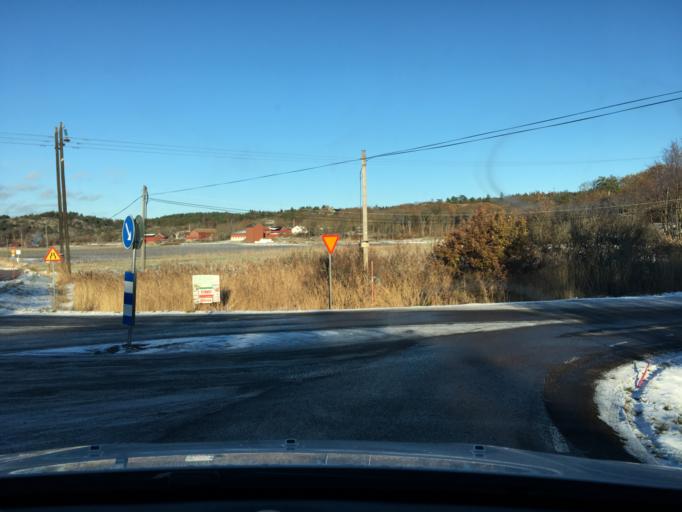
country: SE
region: Vaestra Goetaland
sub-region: Tjorns Kommun
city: Myggenas
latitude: 58.1005
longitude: 11.7081
